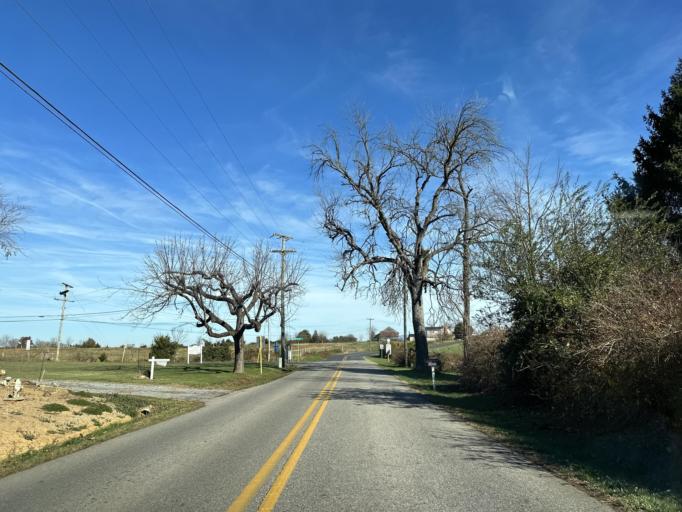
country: US
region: Virginia
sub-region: Augusta County
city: Crimora
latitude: 38.2123
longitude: -78.9009
